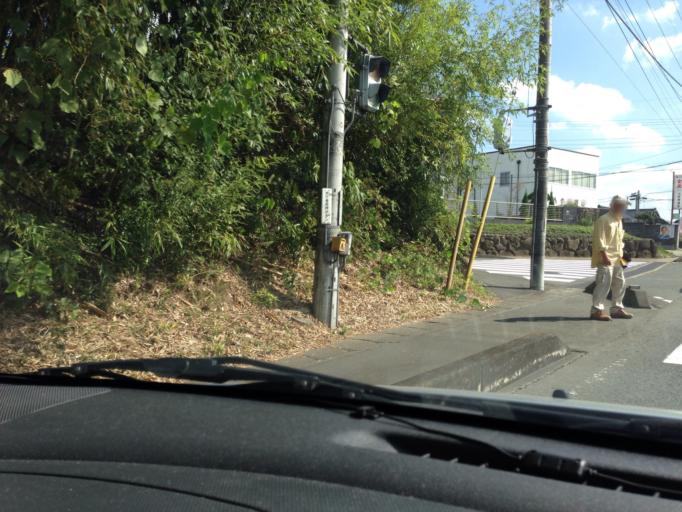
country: JP
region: Ibaraki
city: Mito-shi
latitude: 36.4104
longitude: 140.4271
